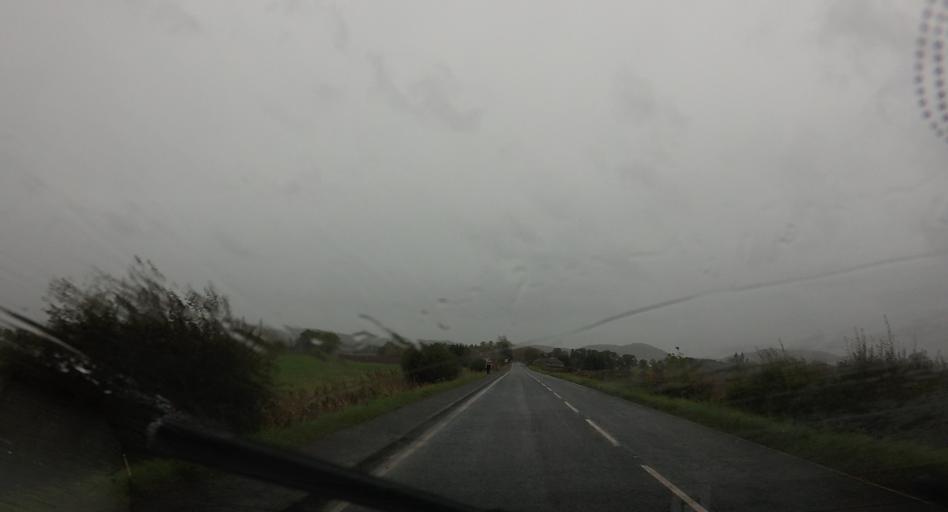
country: GB
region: Scotland
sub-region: Perth and Kinross
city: Coupar Angus
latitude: 56.5419
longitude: -3.2633
